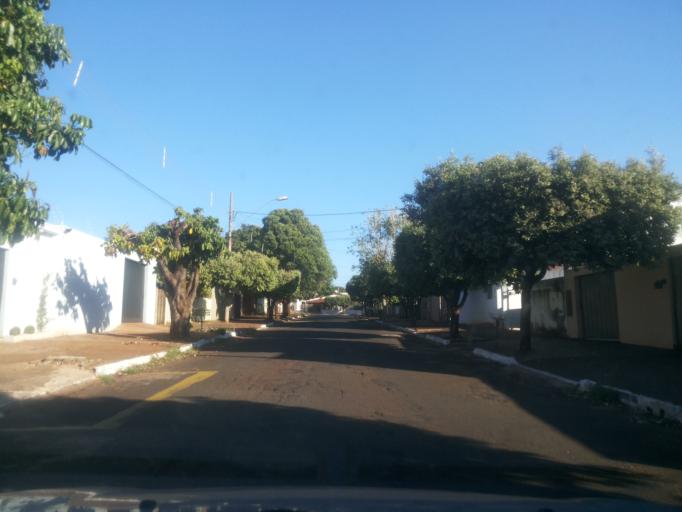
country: BR
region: Minas Gerais
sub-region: Ituiutaba
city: Ituiutaba
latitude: -18.9850
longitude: -49.4675
